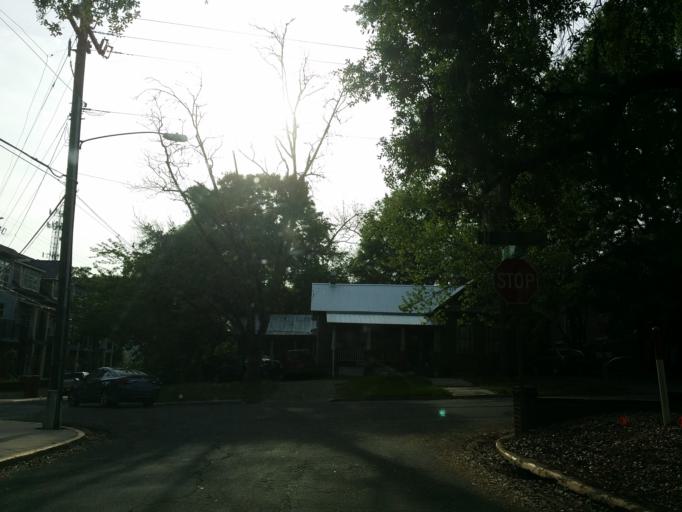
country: US
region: Florida
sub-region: Leon County
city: Tallahassee
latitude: 30.4346
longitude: -84.2859
